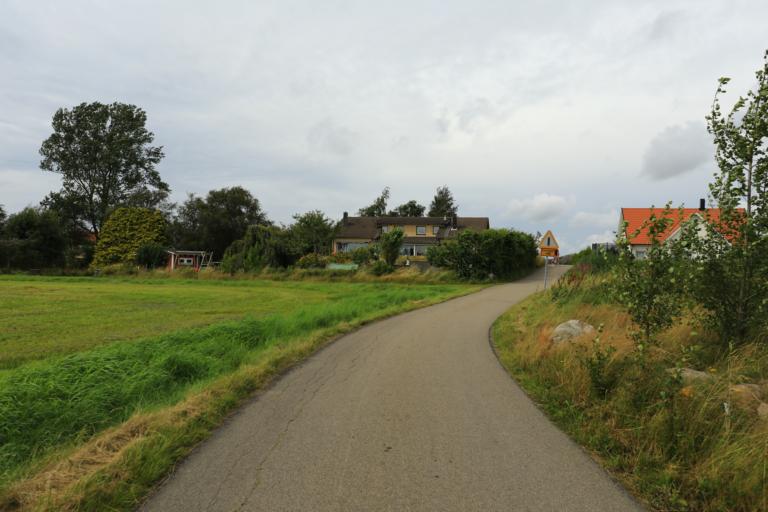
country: SE
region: Halland
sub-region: Varbergs Kommun
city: Varberg
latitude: 57.1476
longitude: 12.2485
